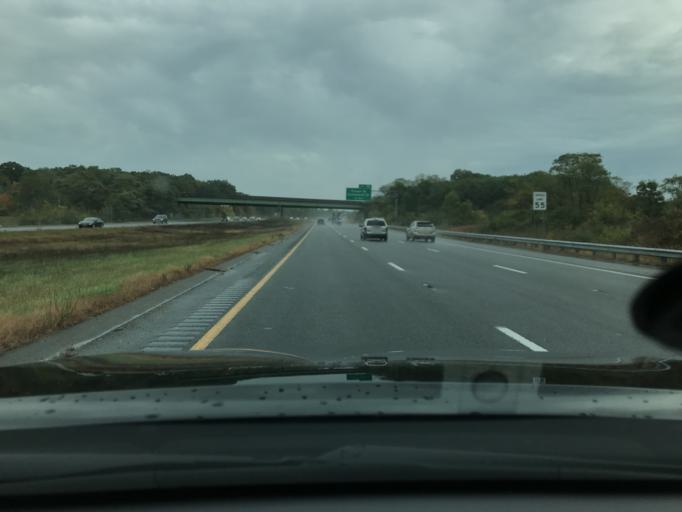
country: US
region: Massachusetts
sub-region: Essex County
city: South Peabody
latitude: 42.5238
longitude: -70.9797
